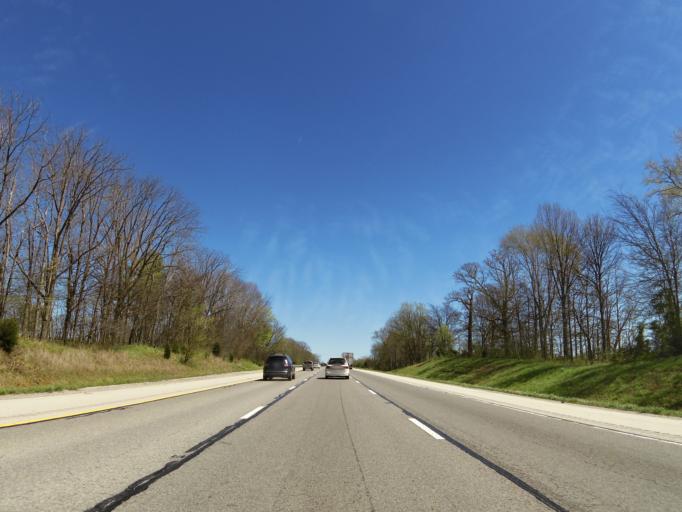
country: US
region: Kentucky
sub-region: Edmonson County
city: Brownsville
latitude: 37.0183
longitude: -86.2653
